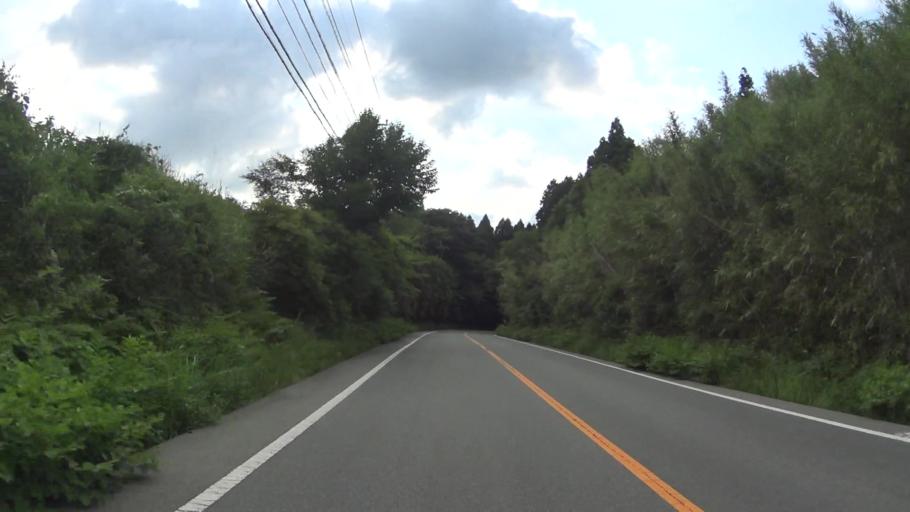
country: JP
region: Kumamoto
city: Aso
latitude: 32.8908
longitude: 131.0222
